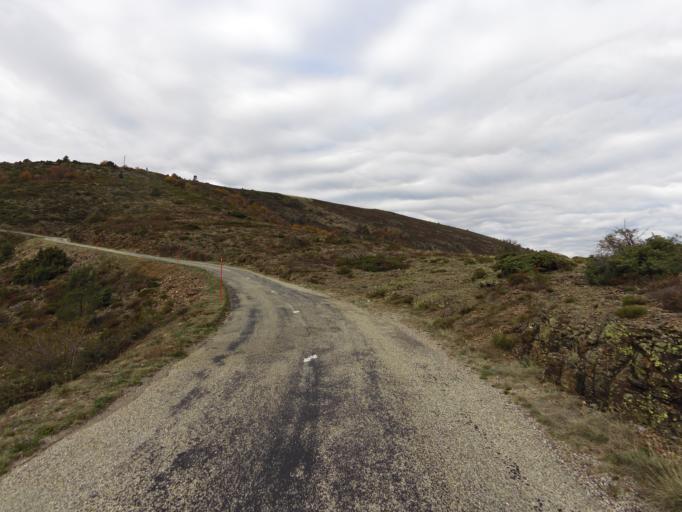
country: FR
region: Rhone-Alpes
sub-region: Departement de l'Ardeche
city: Les Vans
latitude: 44.5104
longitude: 4.0577
